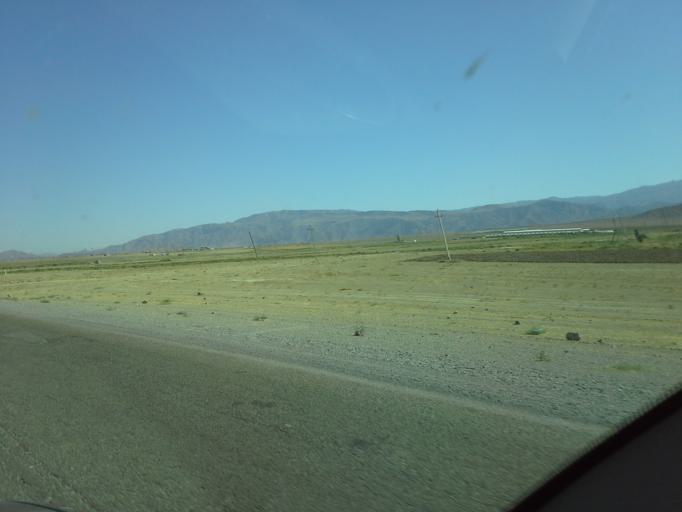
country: TM
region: Ahal
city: Baharly
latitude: 38.4540
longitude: 57.3668
